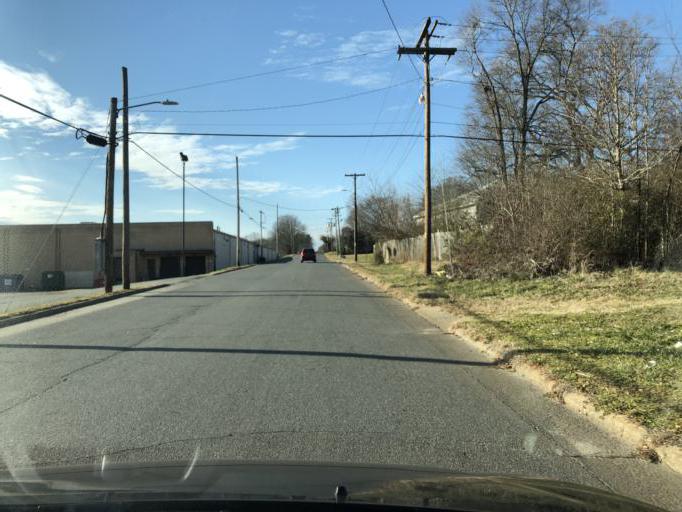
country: US
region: North Carolina
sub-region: Cleveland County
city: Shelby
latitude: 35.2815
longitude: -81.5461
